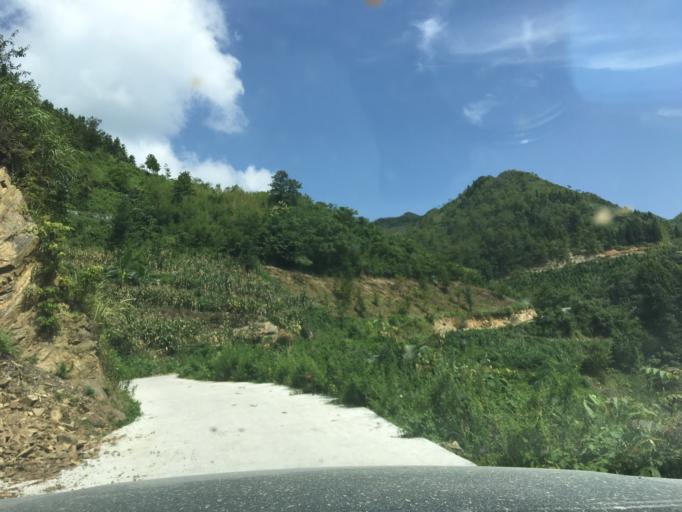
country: CN
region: Guangxi Zhuangzu Zizhiqu
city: Xinzhou
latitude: 24.9661
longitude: 105.6207
